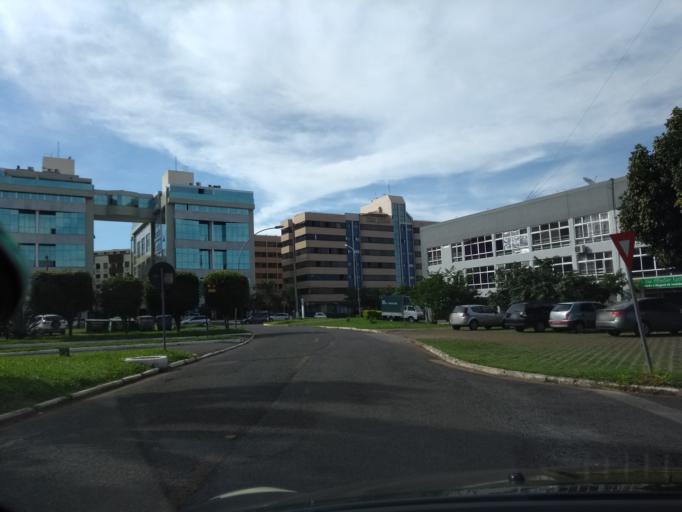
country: BR
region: Federal District
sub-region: Brasilia
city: Brasilia
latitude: -15.7950
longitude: -47.9292
